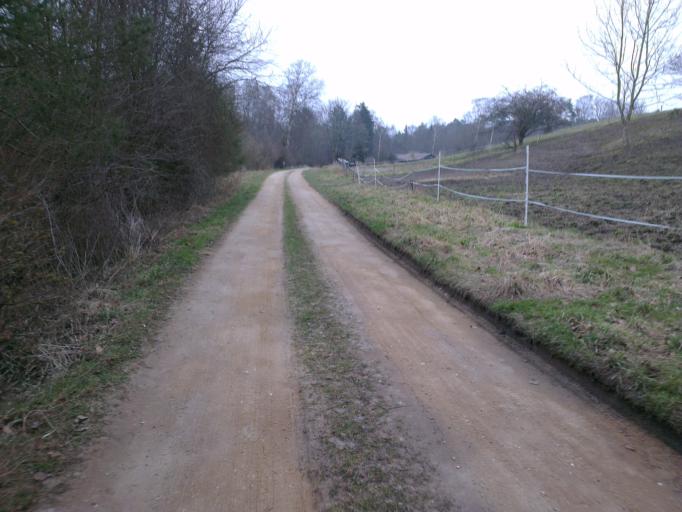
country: DK
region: Capital Region
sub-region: Frederikssund Kommune
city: Frederikssund
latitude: 55.7810
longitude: 12.0338
